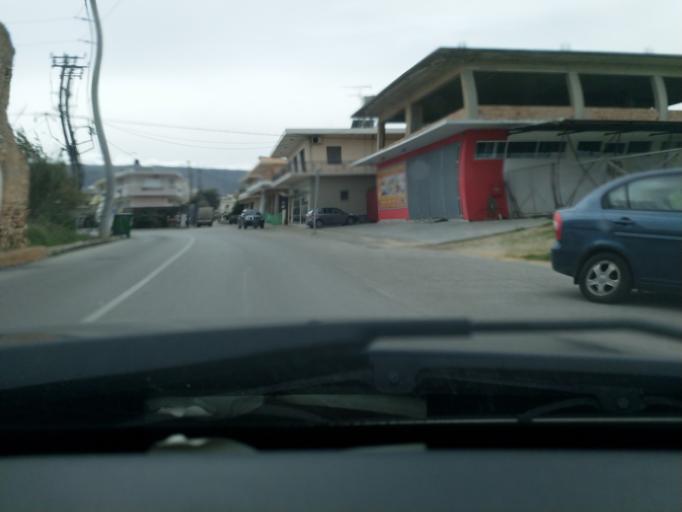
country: GR
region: Crete
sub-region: Nomos Chanias
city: Chania
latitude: 35.4979
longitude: 24.0216
